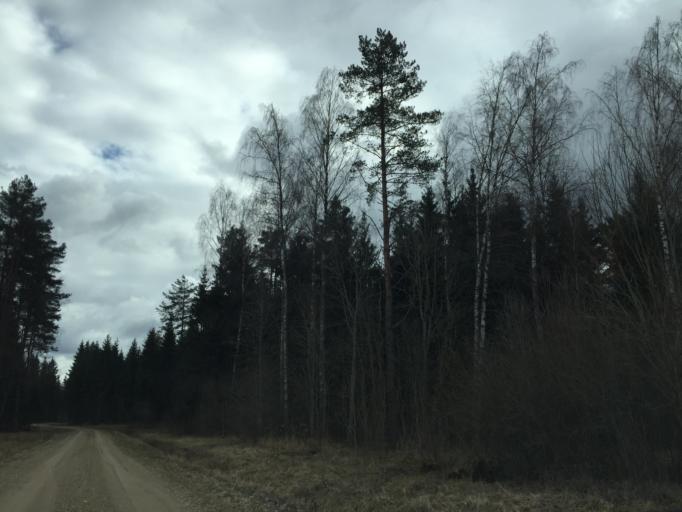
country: LV
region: Akniste
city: Akniste
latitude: 56.0949
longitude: 25.7599
